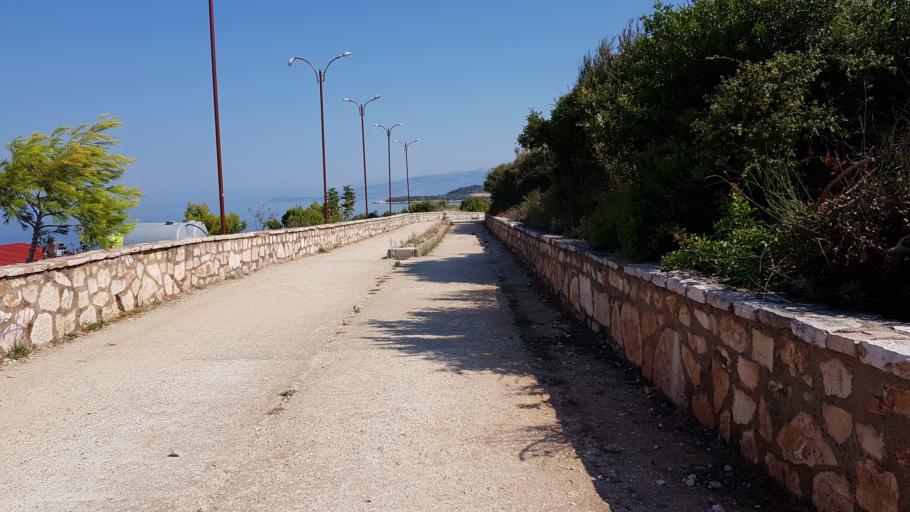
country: AL
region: Vlore
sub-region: Rrethi i Sarandes
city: Xarre
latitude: 39.7764
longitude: 20.0013
